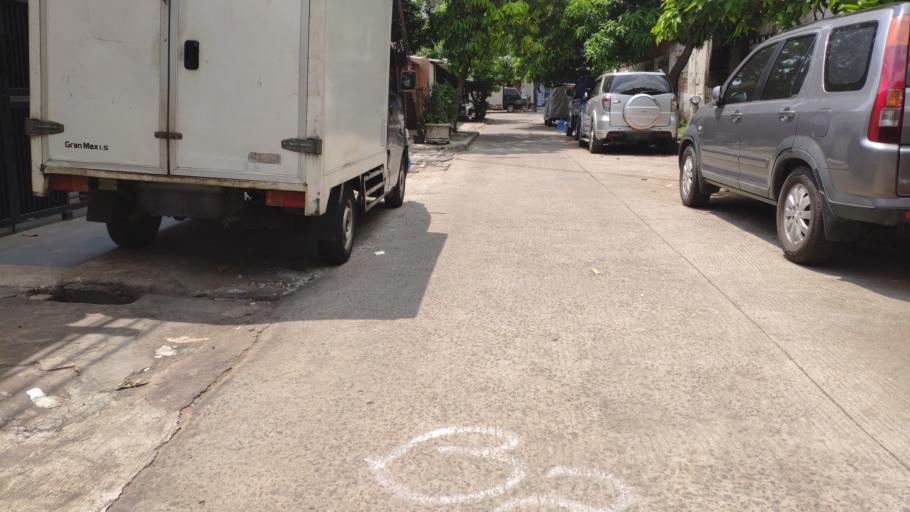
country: ID
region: Jakarta Raya
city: Jakarta
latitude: -6.2130
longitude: 106.8730
